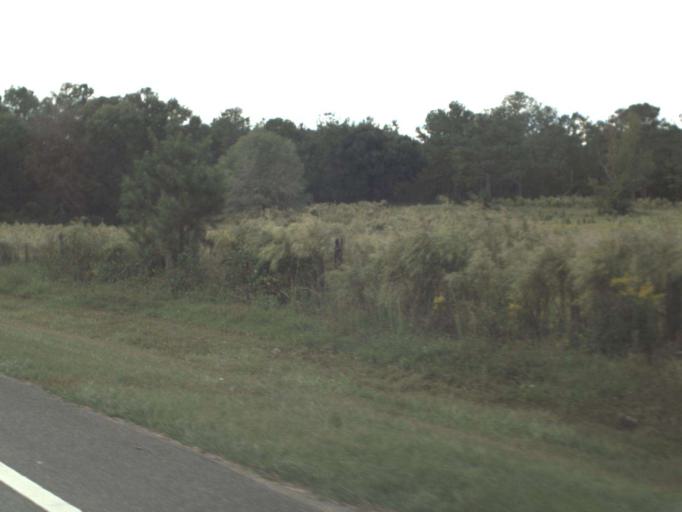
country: US
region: Florida
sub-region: Walton County
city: DeFuniak Springs
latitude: 30.7052
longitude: -85.9340
